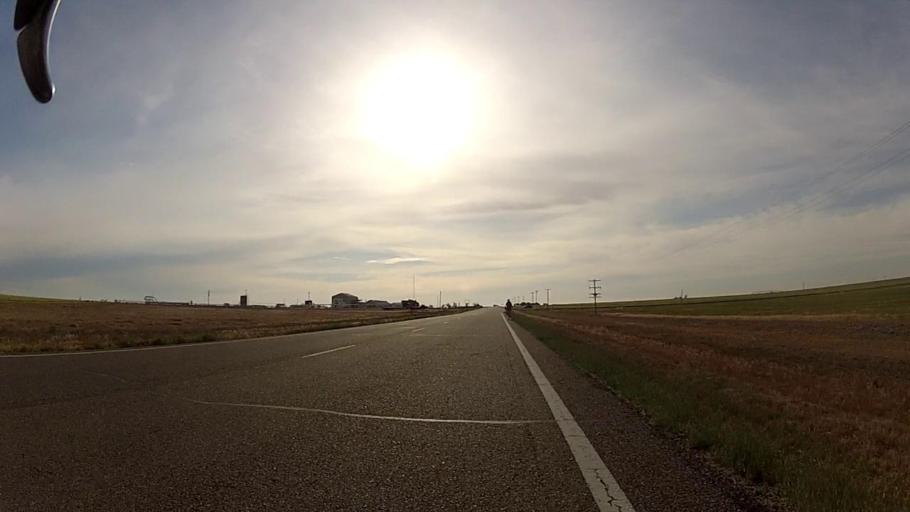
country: US
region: Kansas
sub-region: Grant County
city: Ulysses
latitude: 37.5766
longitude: -101.4927
